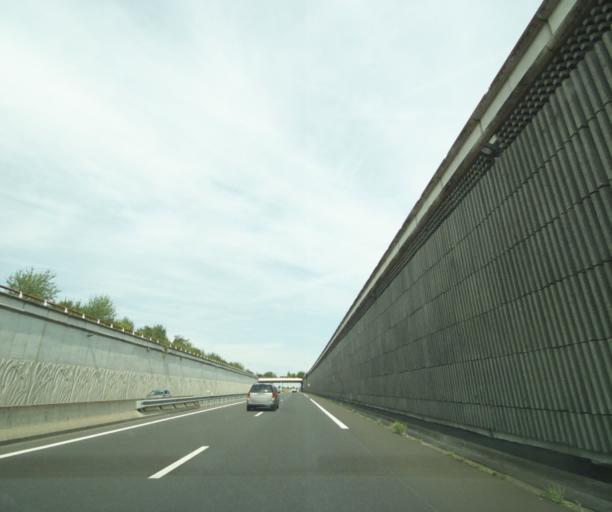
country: FR
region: Centre
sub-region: Departement d'Indre-et-Loire
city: La Membrolle-sur-Choisille
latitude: 47.4301
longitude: 0.6458
